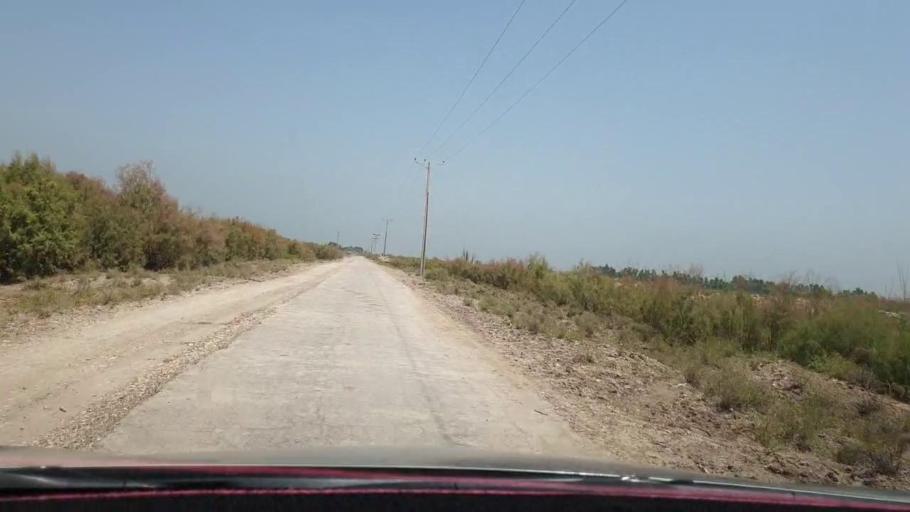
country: PK
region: Sindh
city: Warah
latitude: 27.4328
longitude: 67.7092
